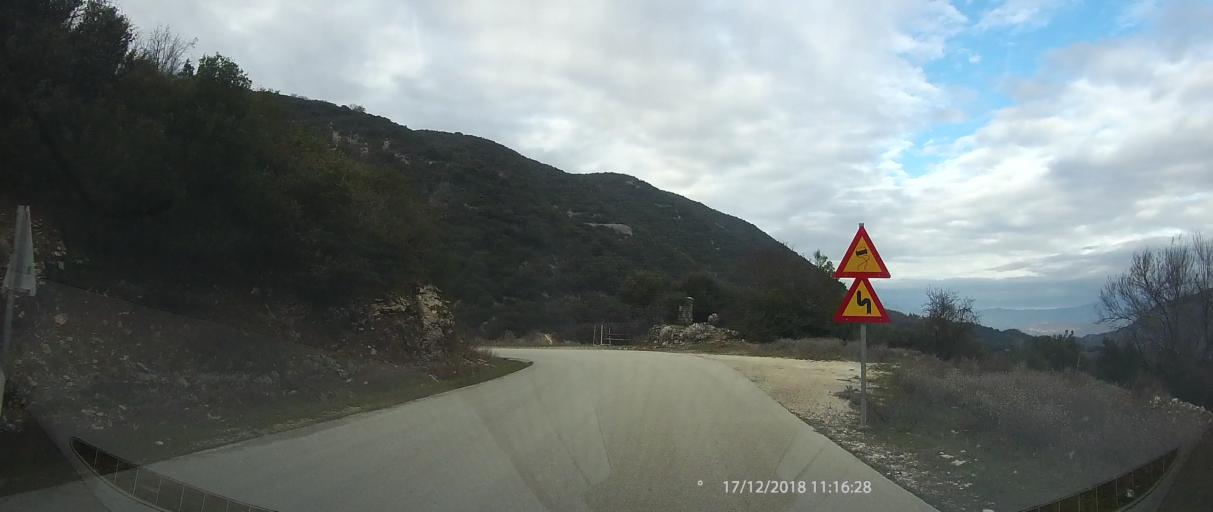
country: GR
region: Epirus
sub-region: Nomos Ioanninon
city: Kalpaki
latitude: 39.9366
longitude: 20.6676
